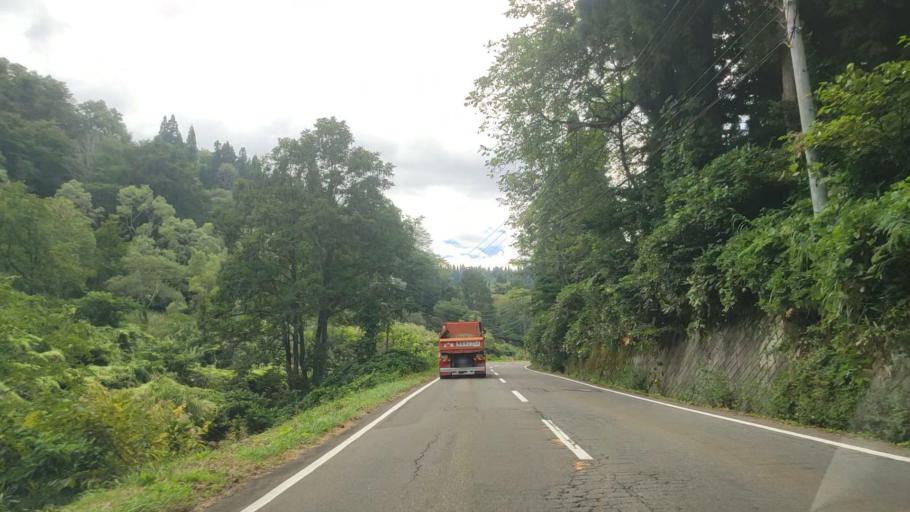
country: JP
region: Nagano
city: Iiyama
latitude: 36.8846
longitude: 138.3212
